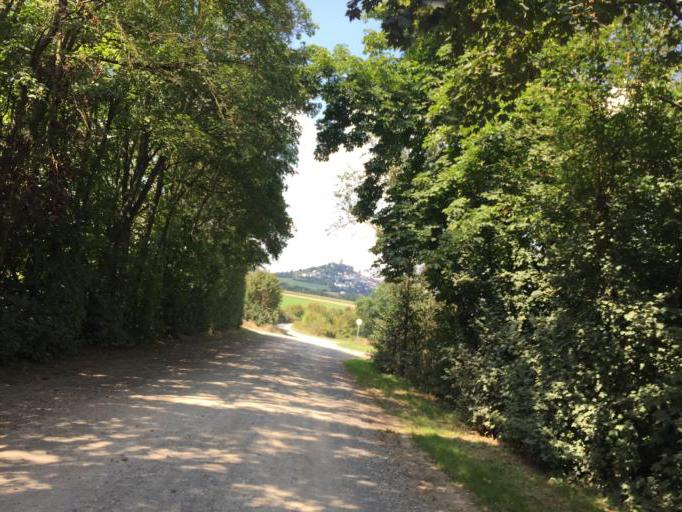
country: DE
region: Hesse
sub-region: Regierungsbezirk Giessen
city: Heuchelheim
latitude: 50.5998
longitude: 8.6481
